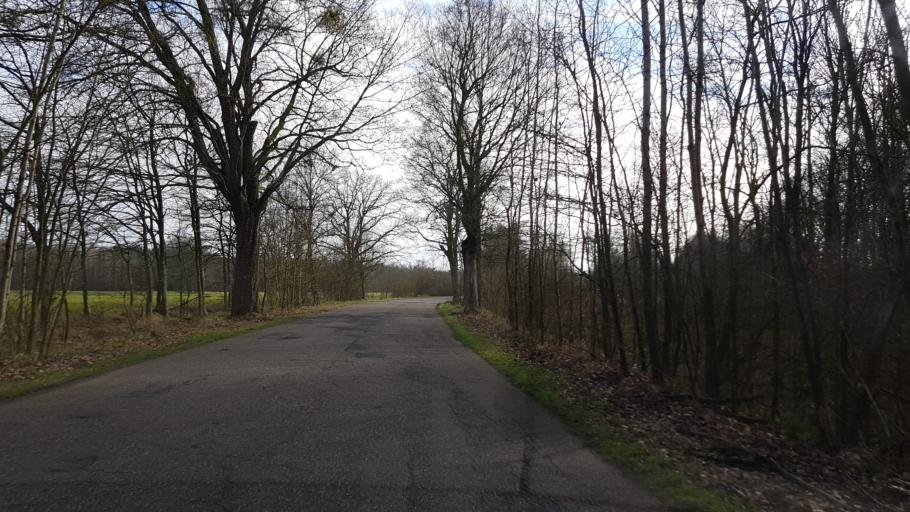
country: PL
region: West Pomeranian Voivodeship
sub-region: Powiat policki
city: Dobra
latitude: 53.5323
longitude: 14.3229
